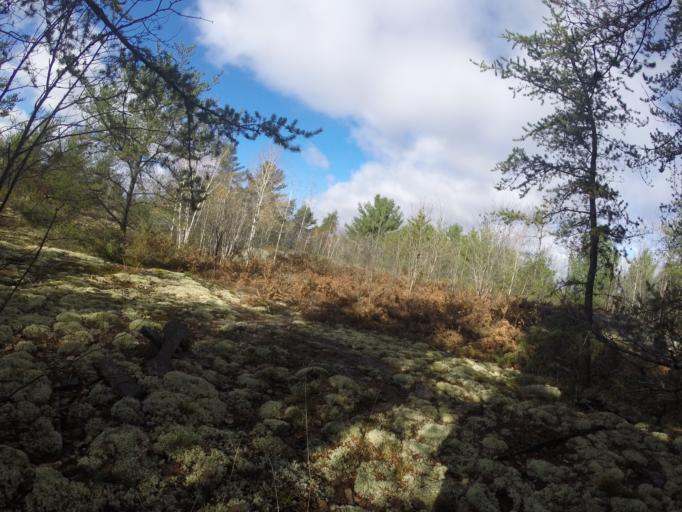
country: CA
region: Ontario
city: Greater Sudbury
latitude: 46.1098
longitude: -80.6532
